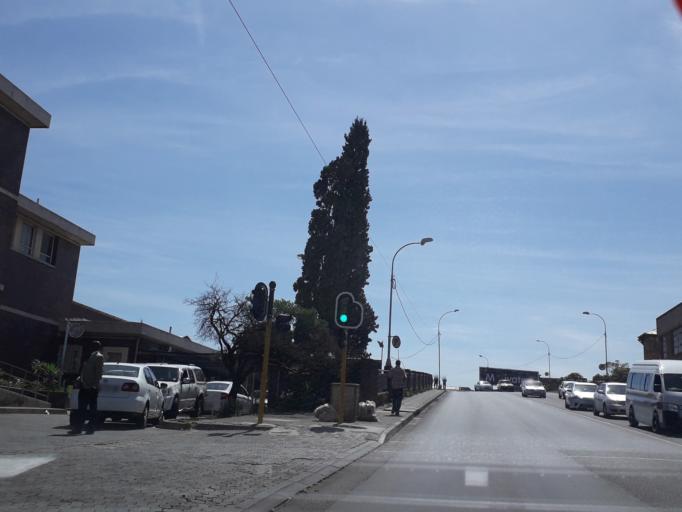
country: ZA
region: Gauteng
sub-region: City of Johannesburg Metropolitan Municipality
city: Johannesburg
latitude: -26.2026
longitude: 28.0606
